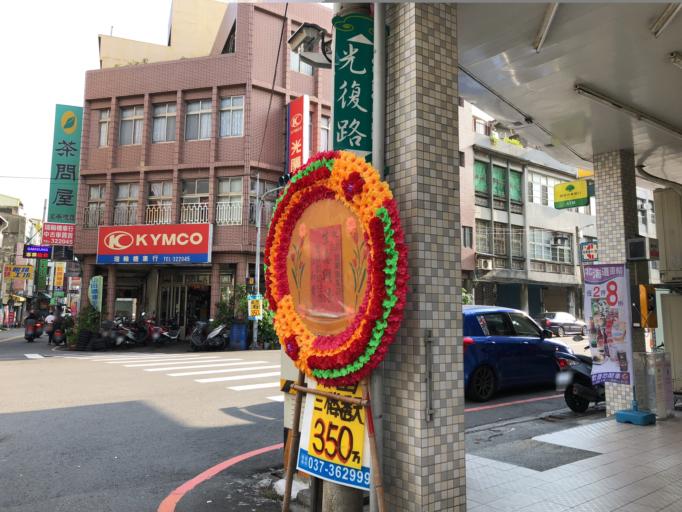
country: TW
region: Taiwan
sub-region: Miaoli
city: Miaoli
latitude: 24.5560
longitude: 120.8160
